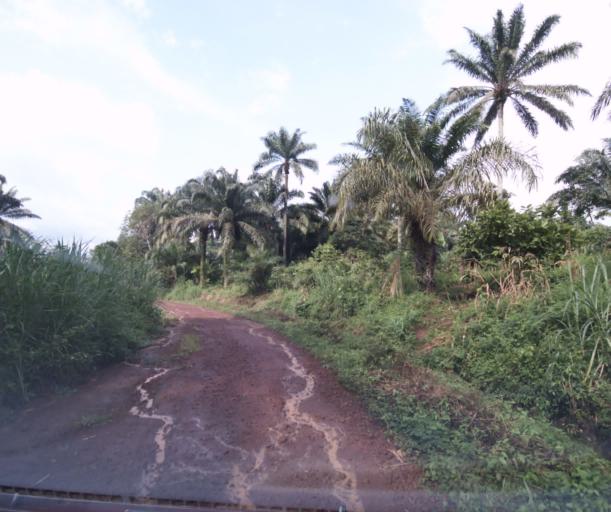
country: CM
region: Littoral
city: Melong
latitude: 5.0596
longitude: 9.9721
